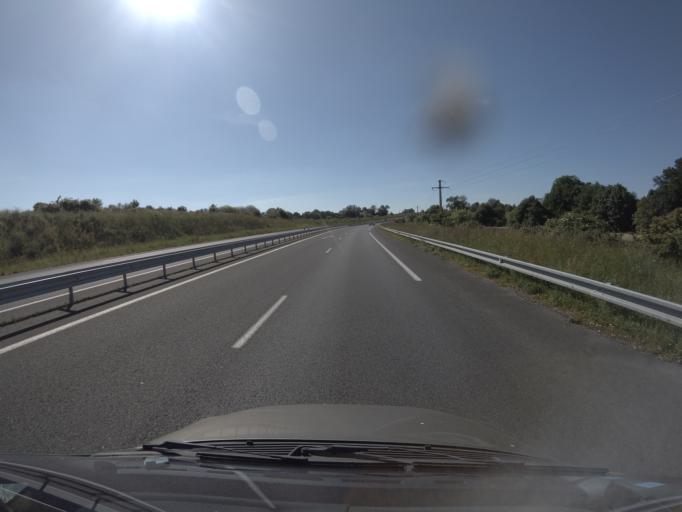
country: FR
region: Pays de la Loire
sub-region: Departement de Maine-et-Loire
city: Coron
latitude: 47.1213
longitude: -0.6561
